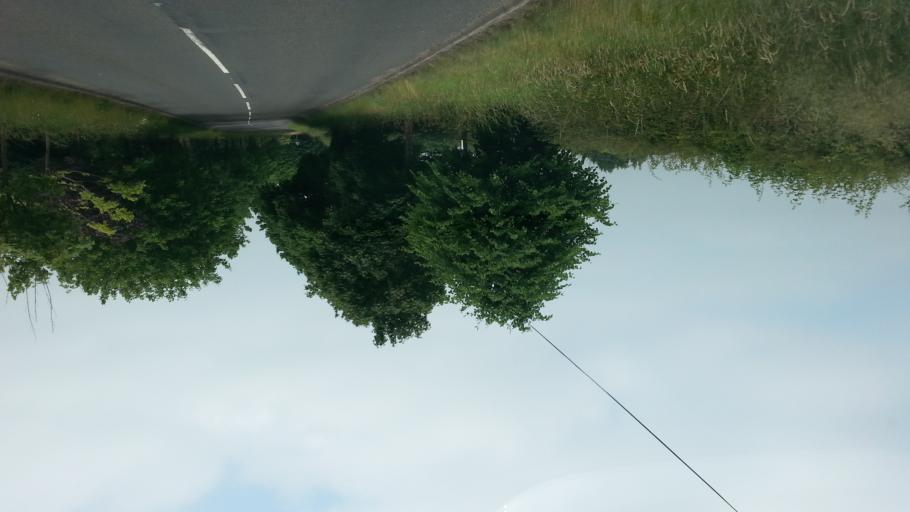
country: GB
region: England
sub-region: Staffordshire
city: Stafford
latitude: 52.8462
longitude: -2.0866
